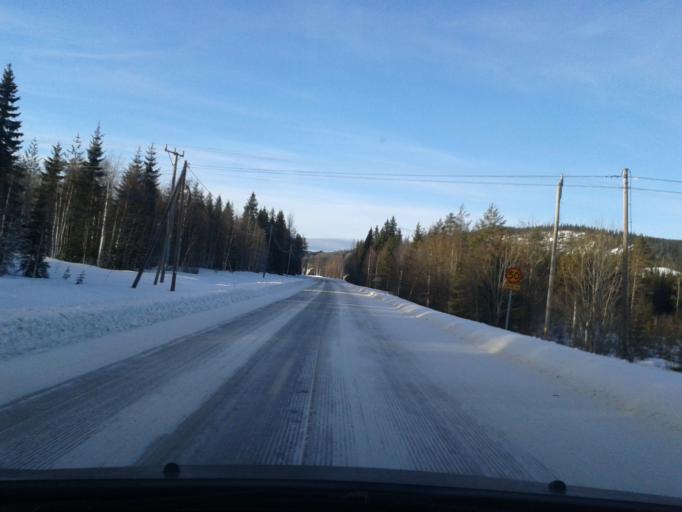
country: SE
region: Vaesterbotten
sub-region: Asele Kommun
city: Asele
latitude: 63.7806
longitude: 17.6639
